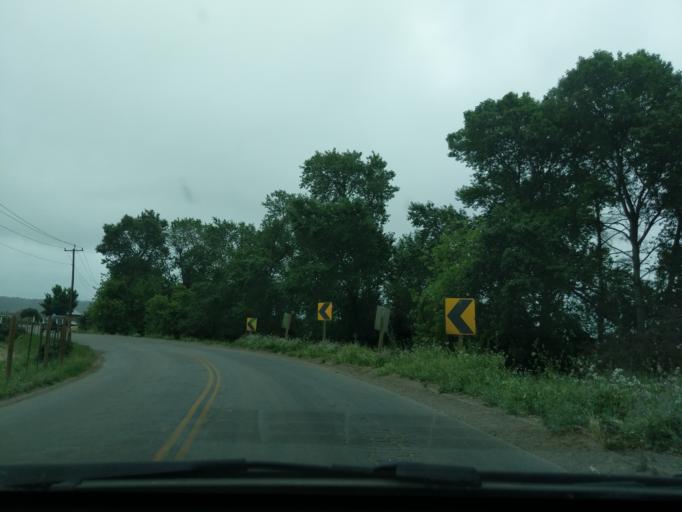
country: US
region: California
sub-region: Santa Cruz County
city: Interlaken
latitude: 36.9271
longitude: -121.7338
